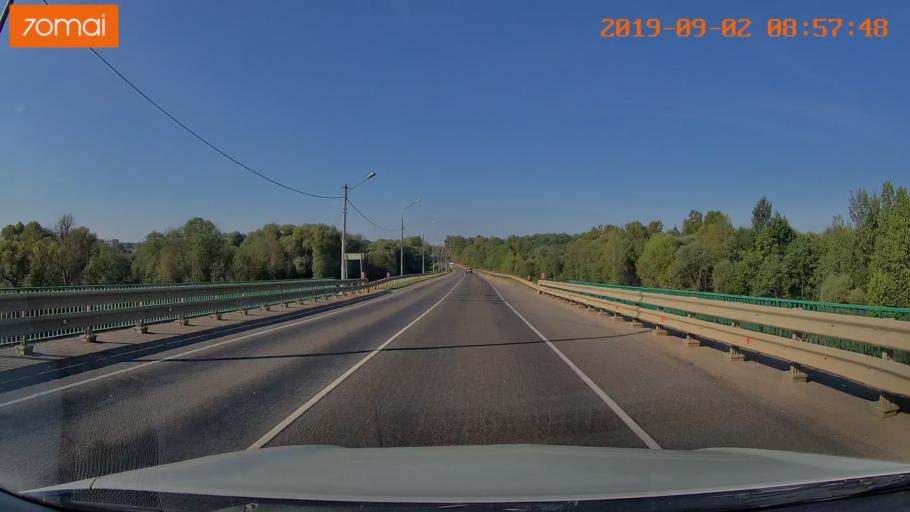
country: RU
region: Kaluga
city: Myatlevo
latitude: 54.9338
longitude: 35.7597
